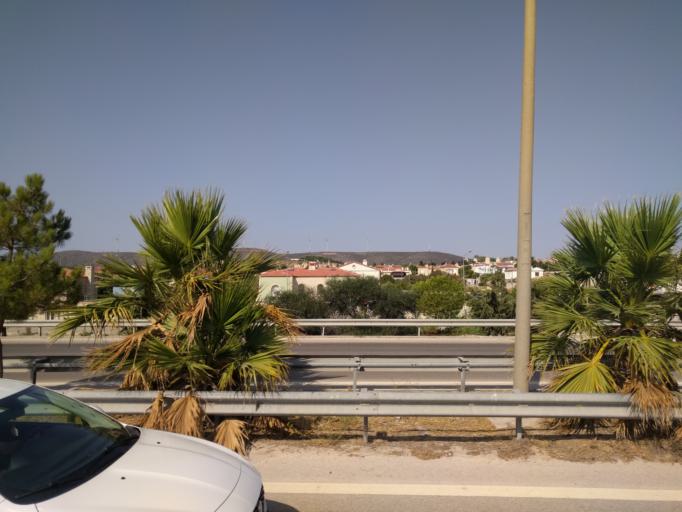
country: TR
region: Izmir
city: Alacati
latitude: 38.2830
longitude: 26.3829
